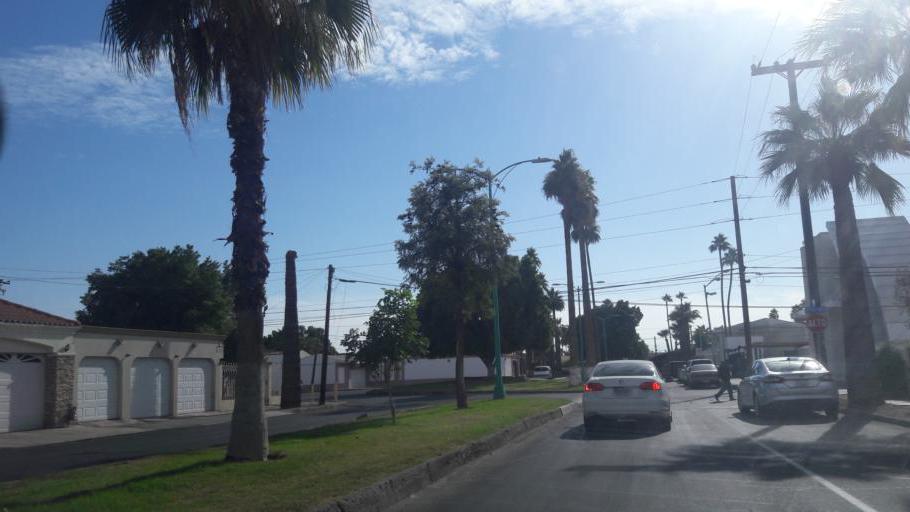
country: MX
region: Baja California
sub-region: Mexicali
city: Mexicali
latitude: 32.6493
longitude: -115.4506
